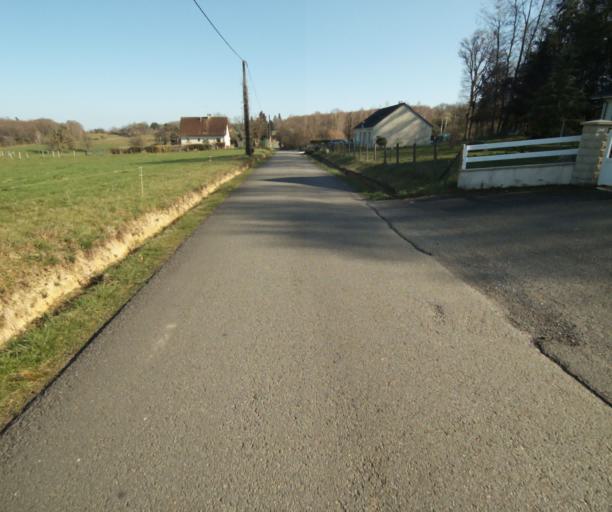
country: FR
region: Limousin
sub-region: Departement de la Correze
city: Saint-Clement
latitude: 45.3141
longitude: 1.6807
